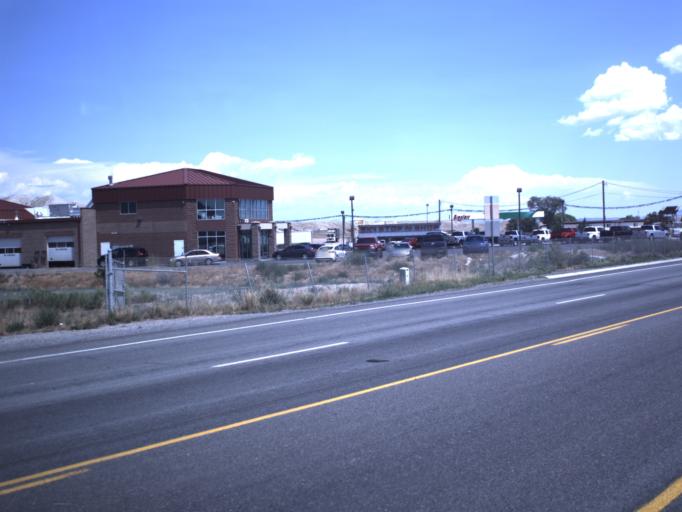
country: US
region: Utah
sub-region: Emery County
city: Huntington
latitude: 39.3349
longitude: -110.9662
